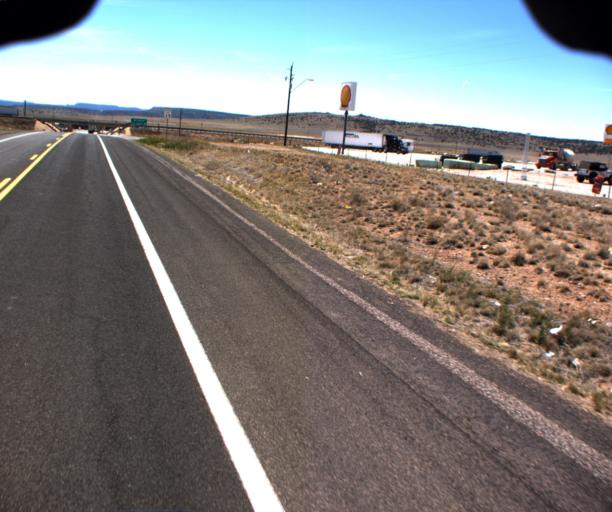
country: US
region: Arizona
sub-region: Yavapai County
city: Paulden
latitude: 35.3124
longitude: -112.8540
